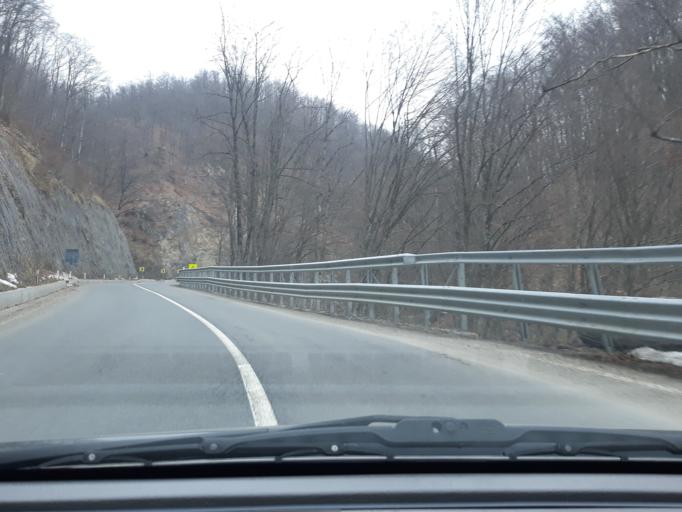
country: RO
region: Bihor
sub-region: Oras Alesd
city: Pestis
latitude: 47.1182
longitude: 22.4103
